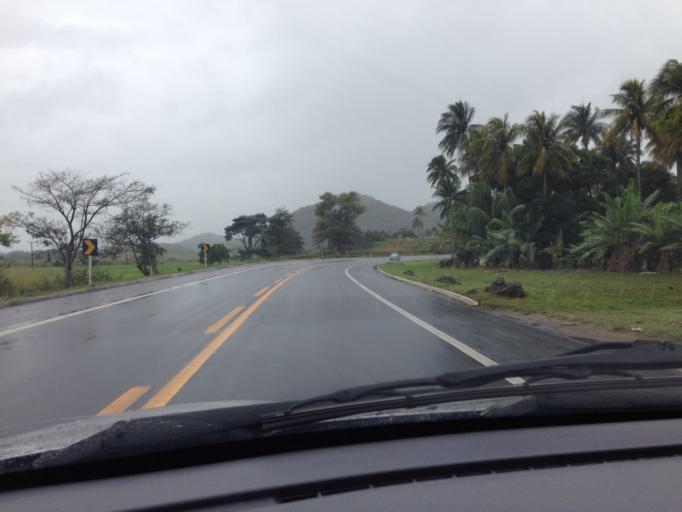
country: BR
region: Espirito Santo
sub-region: Guarapari
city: Guarapari
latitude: -20.6016
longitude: -40.5025
